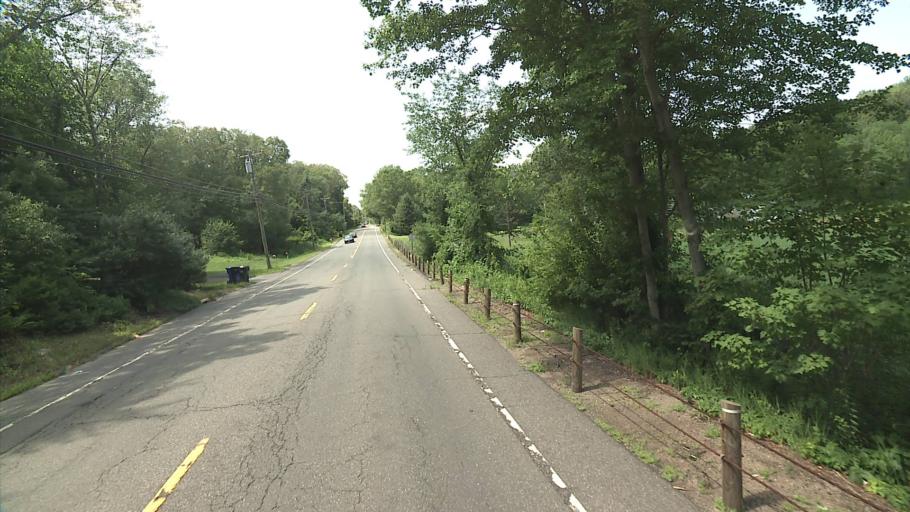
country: US
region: Connecticut
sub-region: Tolland County
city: South Coventry
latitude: 41.7639
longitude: -72.2863
